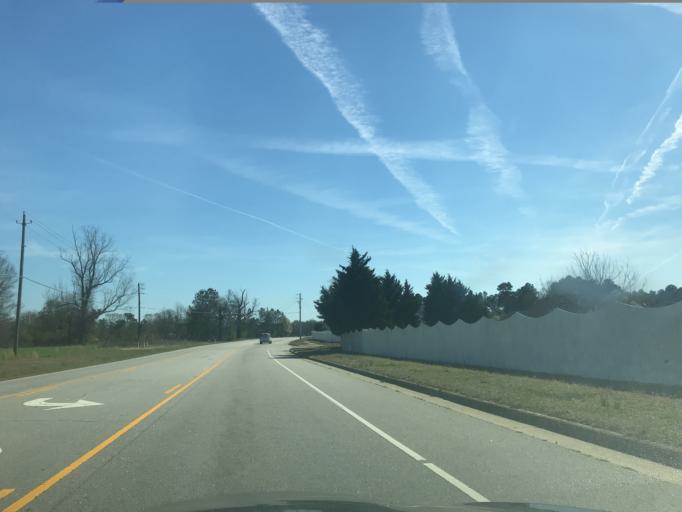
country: US
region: North Carolina
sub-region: Wake County
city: Fuquay-Varina
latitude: 35.5857
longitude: -78.7727
